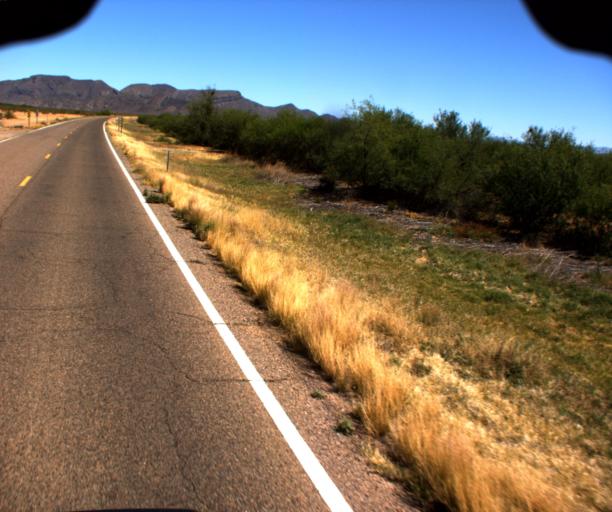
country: US
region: Arizona
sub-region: Yavapai County
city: Congress
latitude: 33.9710
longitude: -113.1415
